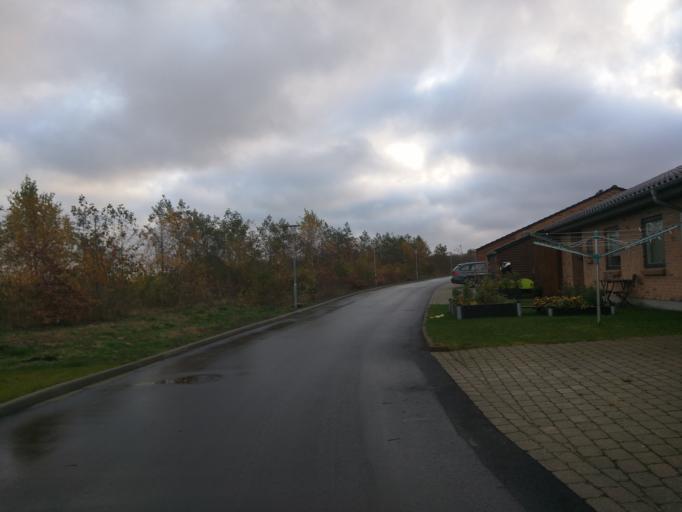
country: DK
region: Central Jutland
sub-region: Viborg Kommune
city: Viborg
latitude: 56.4444
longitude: 9.3624
